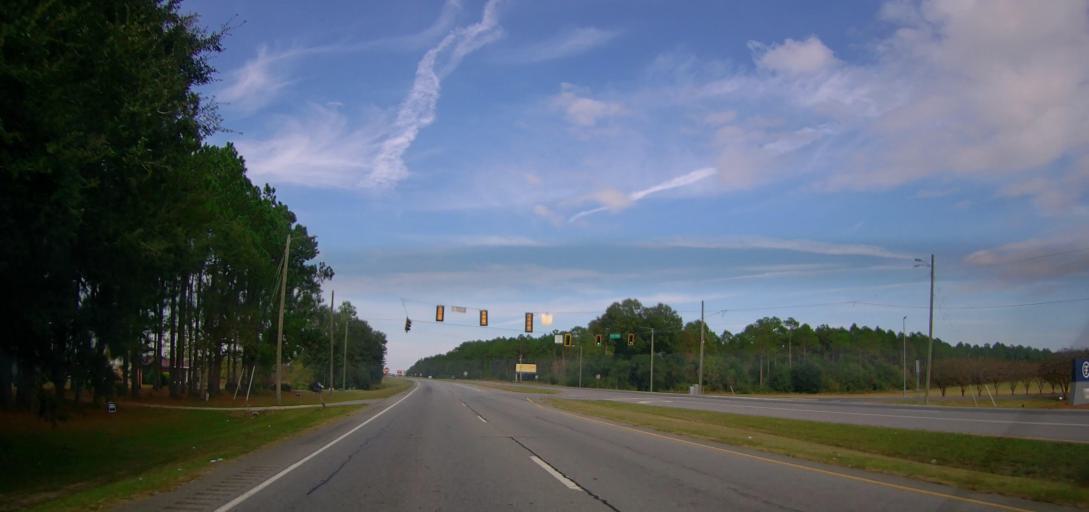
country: US
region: Georgia
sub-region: Mitchell County
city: Camilla
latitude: 31.2805
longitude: -84.1884
